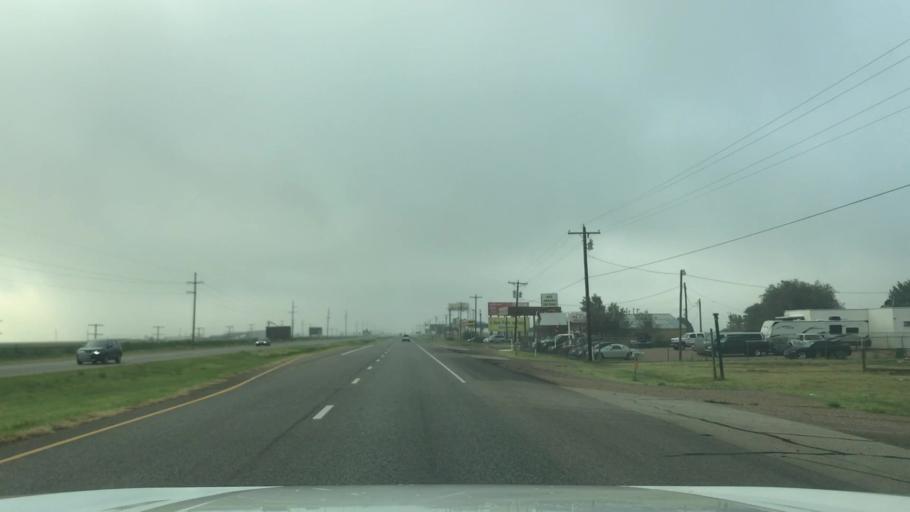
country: US
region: Texas
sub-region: Lubbock County
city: Ransom Canyon
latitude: 33.4962
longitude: -101.7352
